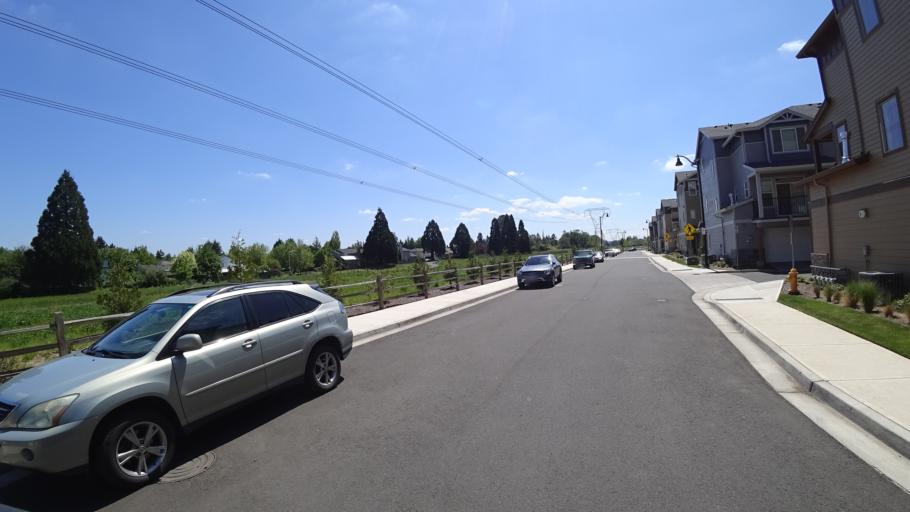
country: US
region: Oregon
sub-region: Washington County
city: Rockcreek
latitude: 45.5181
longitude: -122.8974
